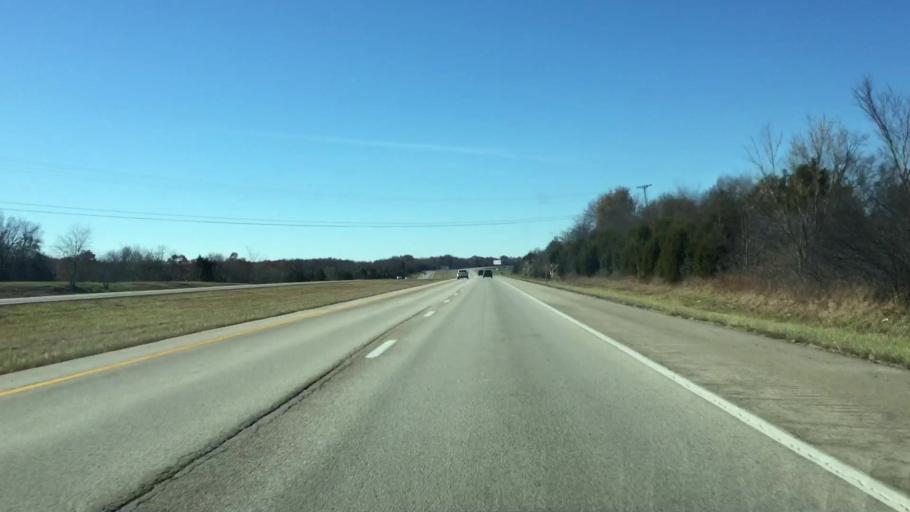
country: US
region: Missouri
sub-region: Miller County
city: Tuscumbia
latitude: 38.3981
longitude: -92.3679
